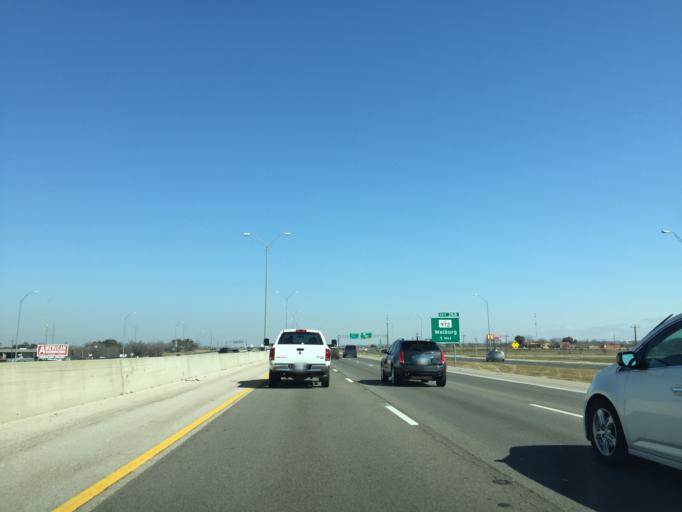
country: US
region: Texas
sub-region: Williamson County
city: Serenada
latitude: 30.6925
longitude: -97.6555
